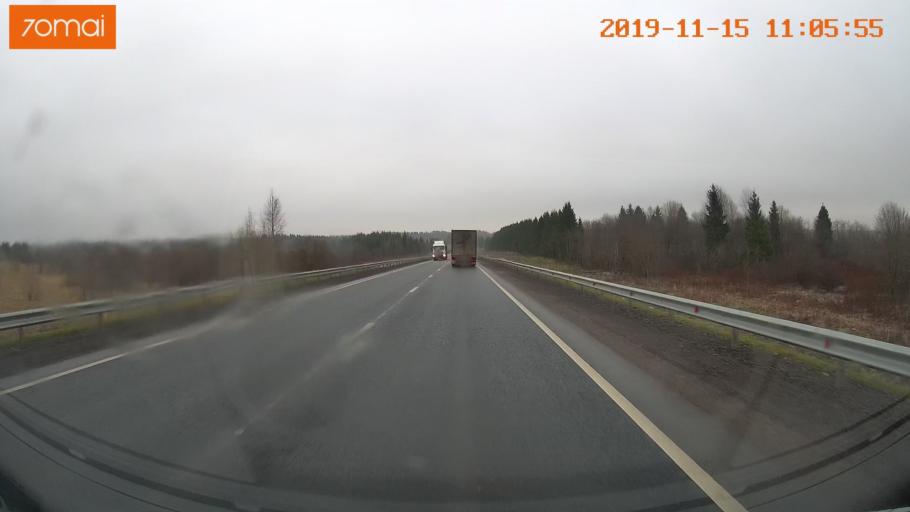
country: RU
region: Vologda
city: Chebsara
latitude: 59.1187
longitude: 39.0146
